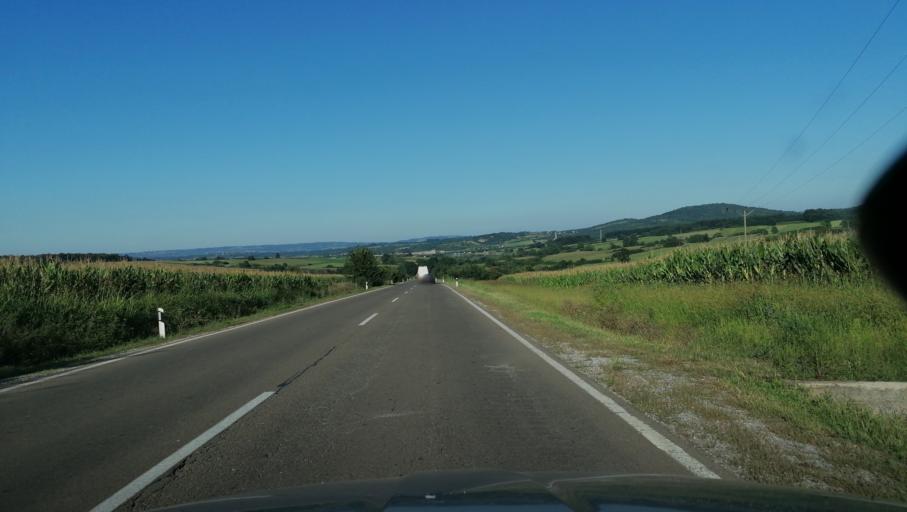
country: RS
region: Central Serbia
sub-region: Sumadijski Okrug
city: Knic
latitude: 43.9157
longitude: 20.6485
